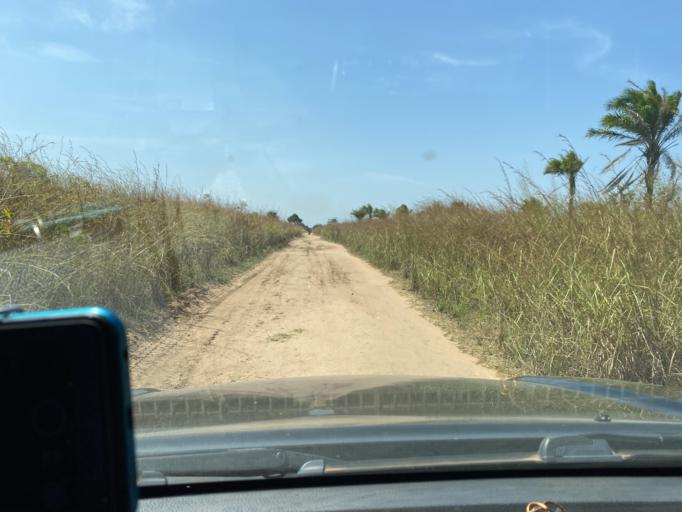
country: CD
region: Kasai-Oriental
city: Kabinda
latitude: -5.8843
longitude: 24.8495
